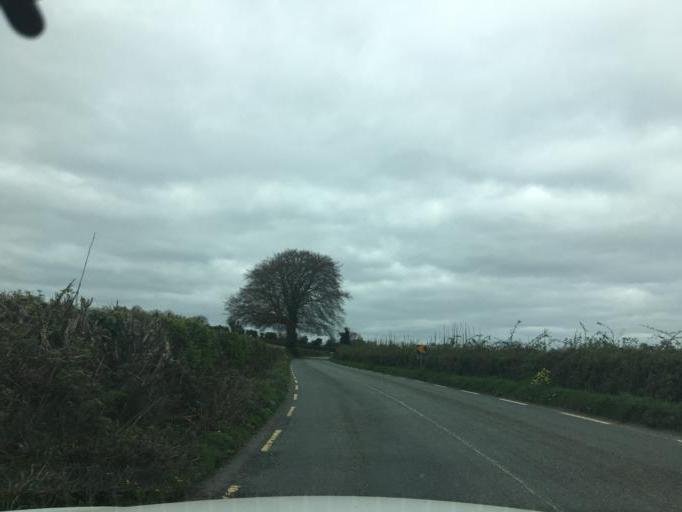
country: IE
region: Leinster
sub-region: Loch Garman
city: New Ross
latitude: 52.4389
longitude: -6.9686
